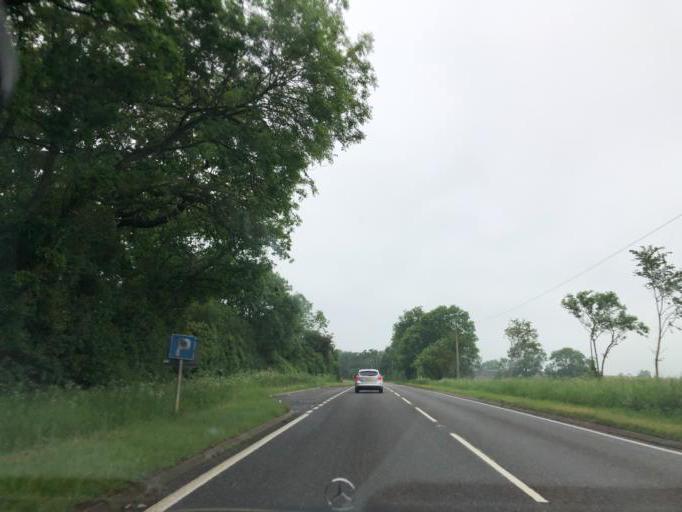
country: GB
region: England
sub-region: Warwickshire
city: Wellesbourne Mountford
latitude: 52.2280
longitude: -1.5385
